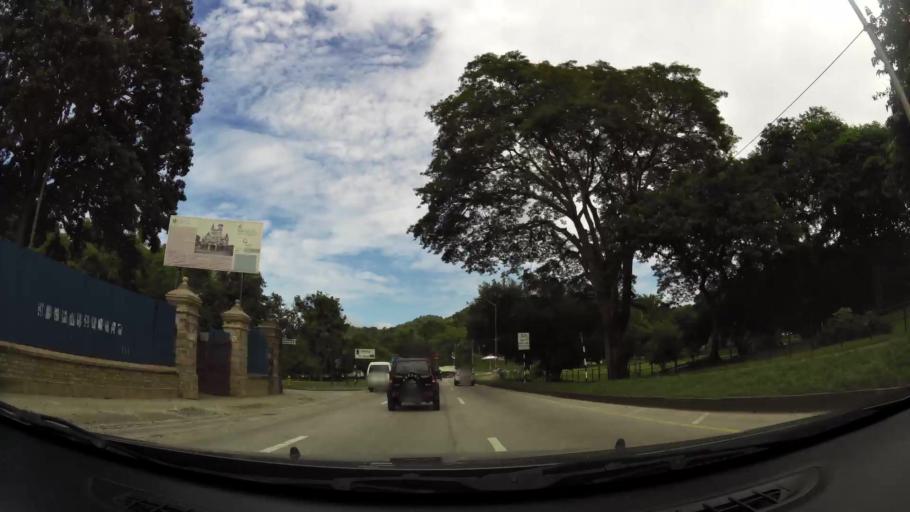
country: TT
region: City of Port of Spain
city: Port-of-Spain
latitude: 10.6726
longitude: -61.5186
